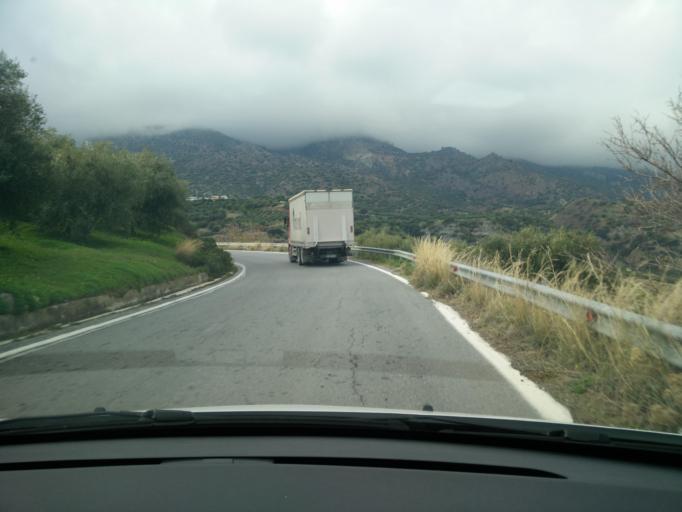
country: GR
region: Crete
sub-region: Nomos Lasithiou
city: Gra Liyia
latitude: 35.0221
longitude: 25.5732
